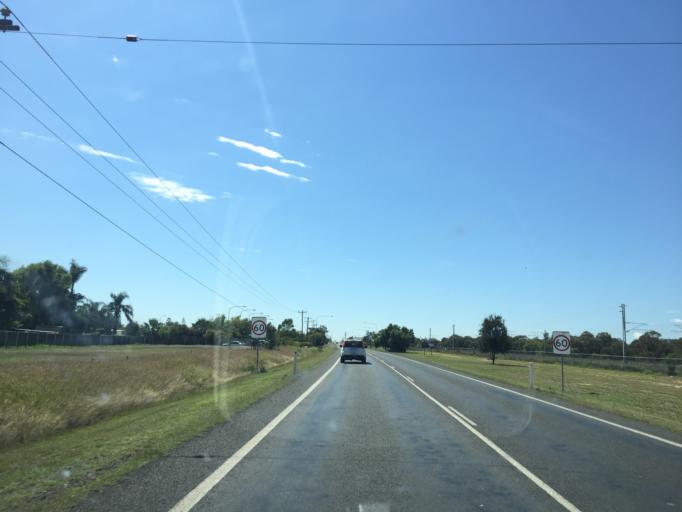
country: AU
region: Queensland
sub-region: Central Highlands
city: Blackwater
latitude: -23.5857
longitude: 148.8691
